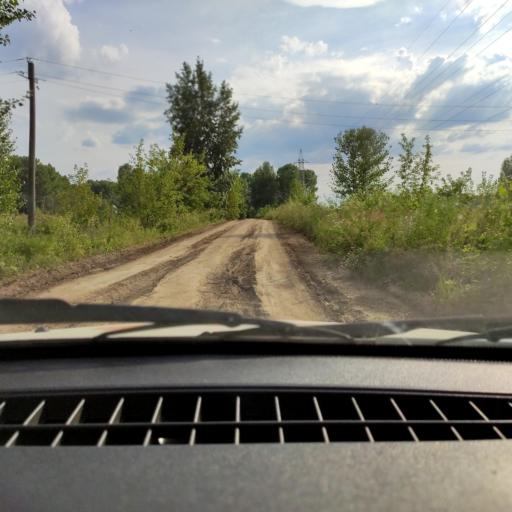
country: RU
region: Bashkortostan
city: Mikhaylovka
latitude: 54.9201
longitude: 55.9341
